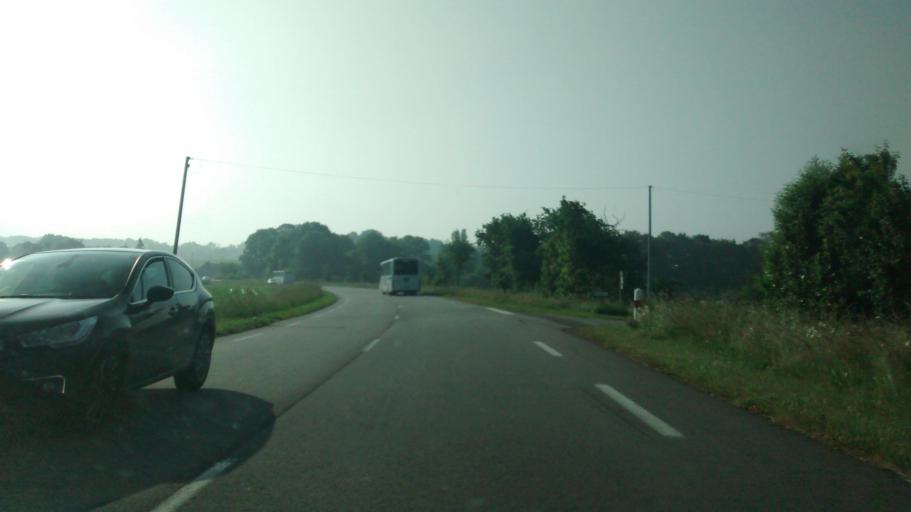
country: FR
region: Brittany
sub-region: Departement du Morbihan
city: Malestroit
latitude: 47.8079
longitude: -2.3331
